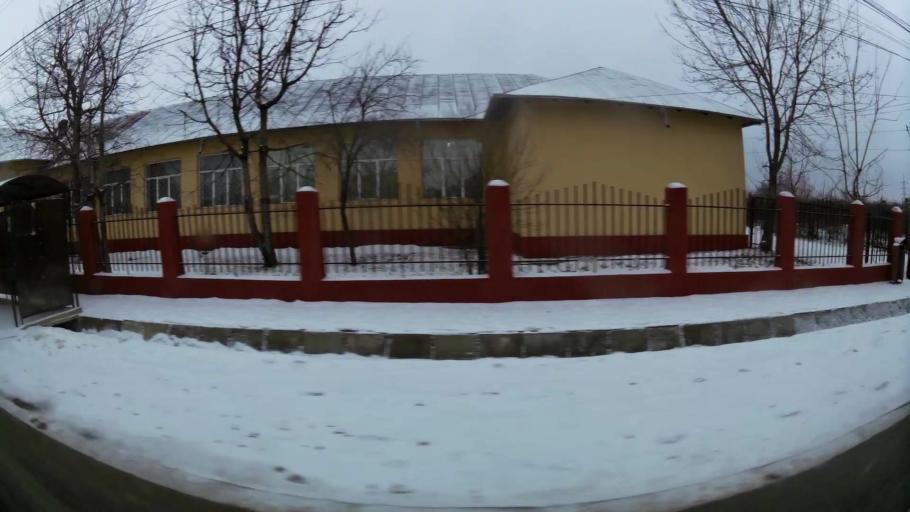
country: RO
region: Prahova
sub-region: Comuna Berceni
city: Corlatesti
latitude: 44.9171
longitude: 26.0826
